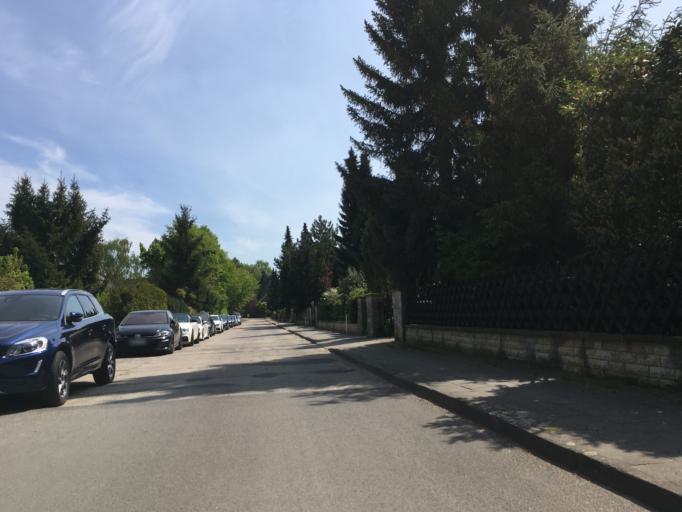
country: DE
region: Berlin
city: Blankenfelde
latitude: 52.6433
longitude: 13.3848
